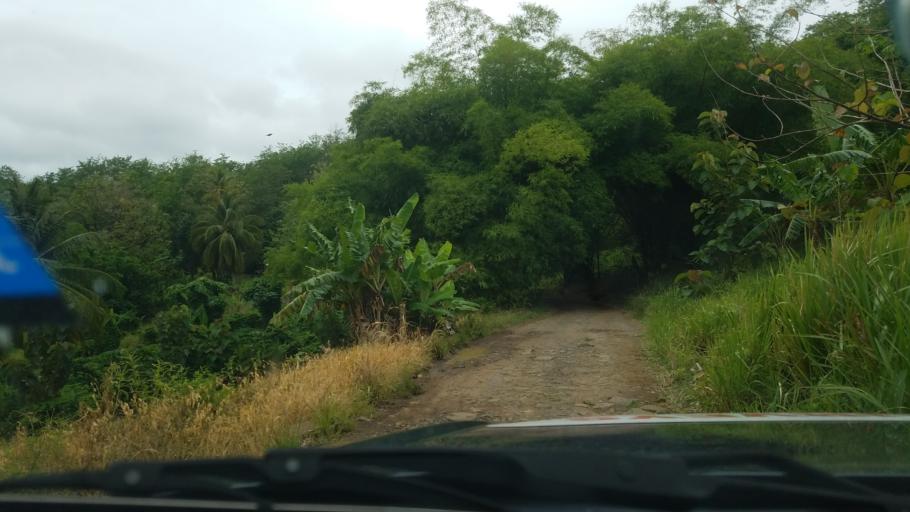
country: LC
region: Castries Quarter
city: Bisee
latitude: 14.0153
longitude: -60.9147
